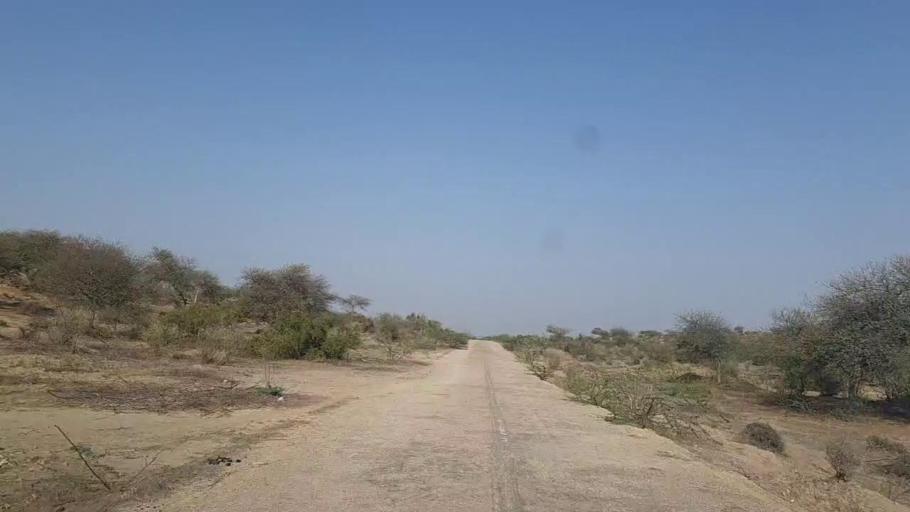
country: PK
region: Sindh
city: Naukot
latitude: 24.6019
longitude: 69.3275
